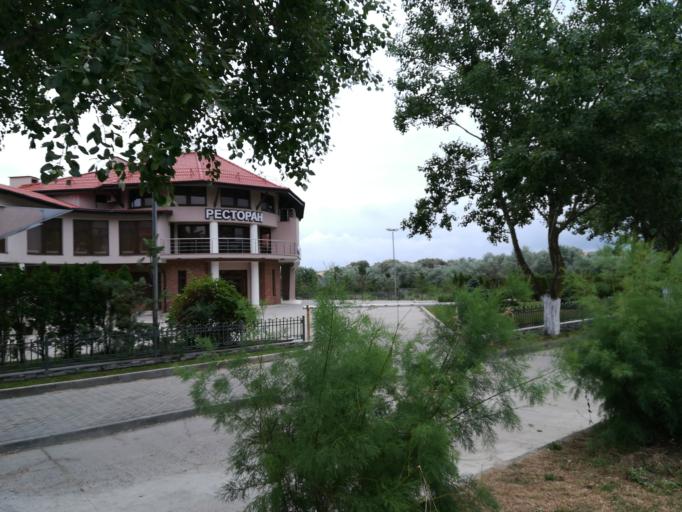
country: RU
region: Krasnodarskiy
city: Vityazevo
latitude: 44.9883
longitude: 37.2451
